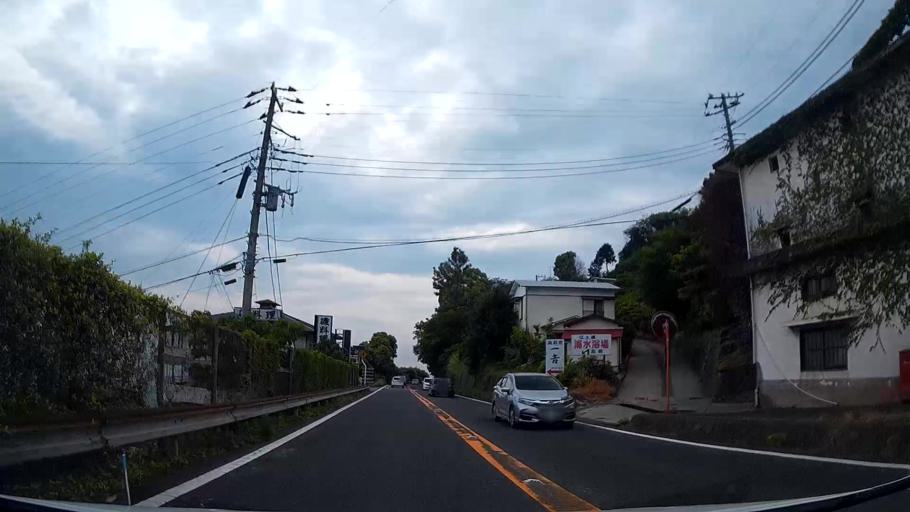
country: JP
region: Kanagawa
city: Odawara
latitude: 35.1909
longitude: 139.1379
